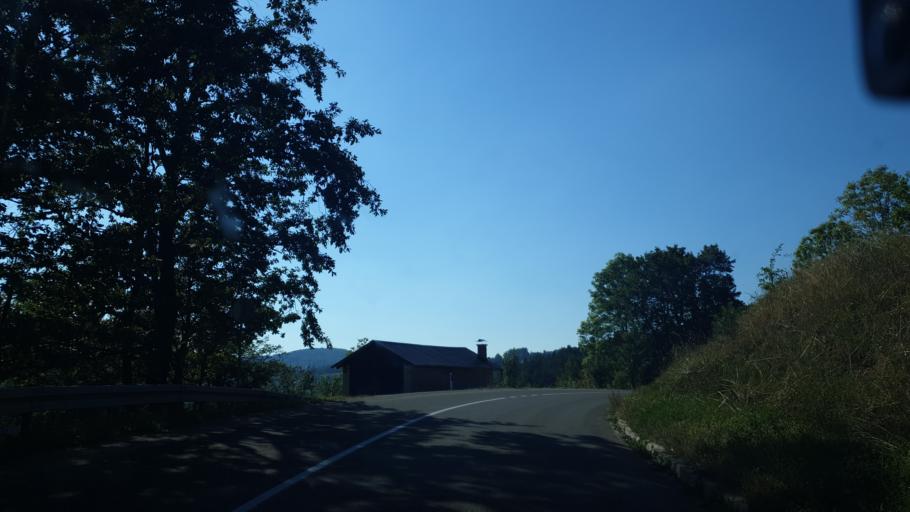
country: RS
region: Central Serbia
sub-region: Zlatiborski Okrug
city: Cajetina
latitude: 43.7225
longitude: 19.8141
